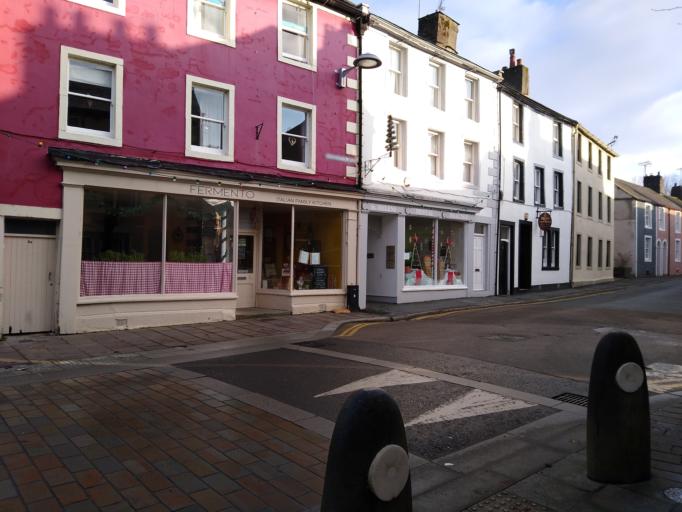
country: GB
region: England
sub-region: Cumbria
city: Cockermouth
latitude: 54.6640
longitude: -3.3600
